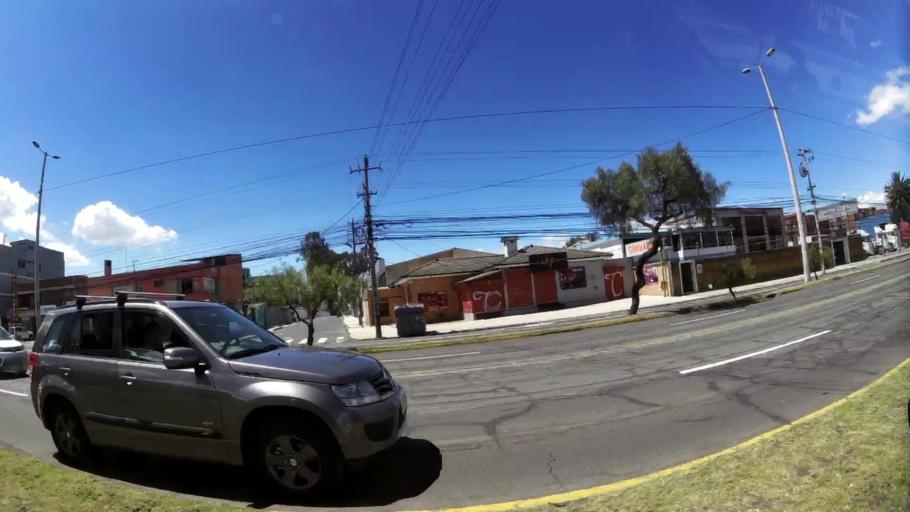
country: EC
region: Pichincha
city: Quito
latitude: -0.1513
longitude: -78.4843
